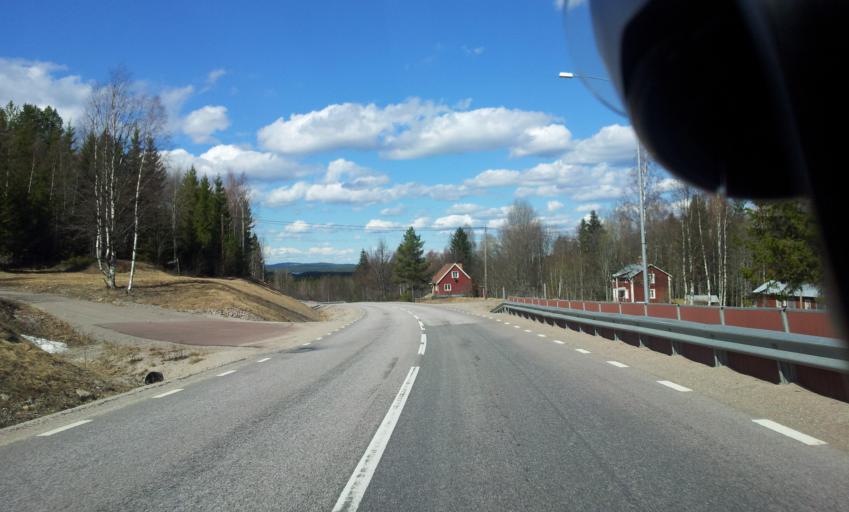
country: SE
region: Gaevleborg
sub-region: Bollnas Kommun
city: Vittsjo
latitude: 61.1511
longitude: 15.8880
